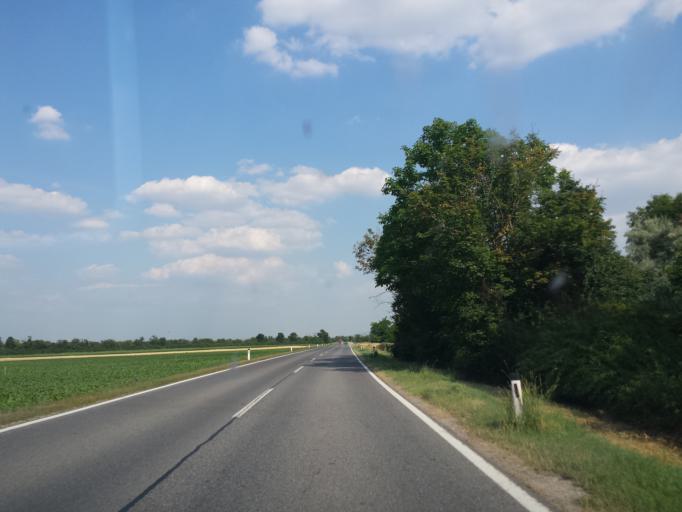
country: AT
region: Lower Austria
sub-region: Politischer Bezirk Ganserndorf
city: Obersiebenbrunn
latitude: 48.2628
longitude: 16.6811
